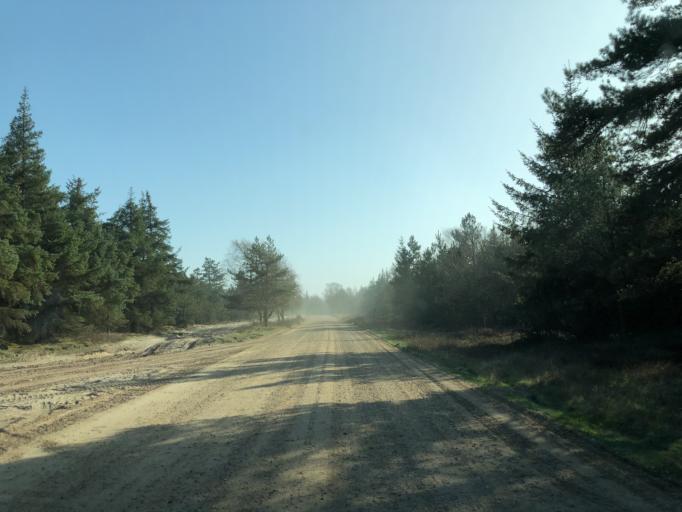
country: DK
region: South Denmark
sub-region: Varde Kommune
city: Oksbol
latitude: 55.6164
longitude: 8.1674
